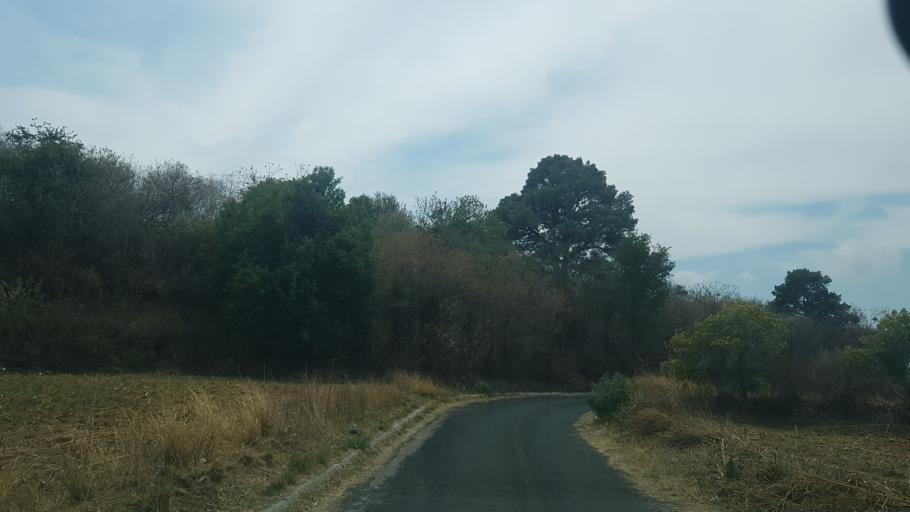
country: MX
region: Puebla
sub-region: Atzitzihuacan
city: Santiago Atzitzihuacan
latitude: 18.8464
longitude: -98.6086
